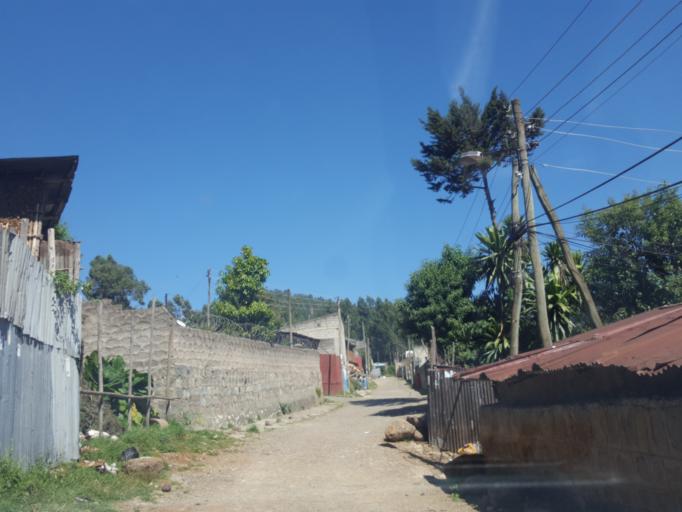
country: ET
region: Adis Abeba
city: Addis Ababa
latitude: 9.0585
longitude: 38.7456
